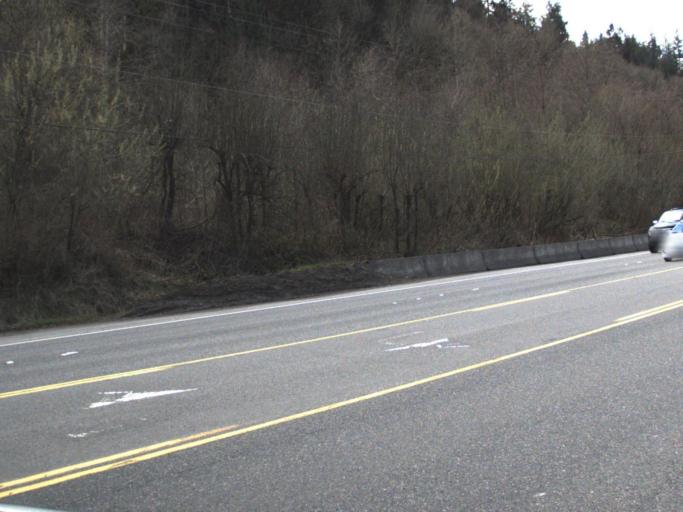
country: US
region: Washington
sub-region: King County
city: East Renton Highlands
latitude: 47.4632
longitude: -122.1131
